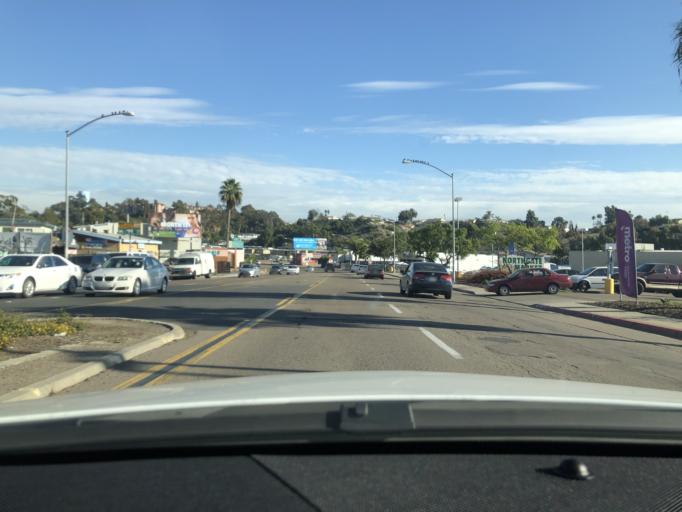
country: US
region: California
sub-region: San Diego County
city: Lemon Grove
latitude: 32.7483
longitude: -117.0780
